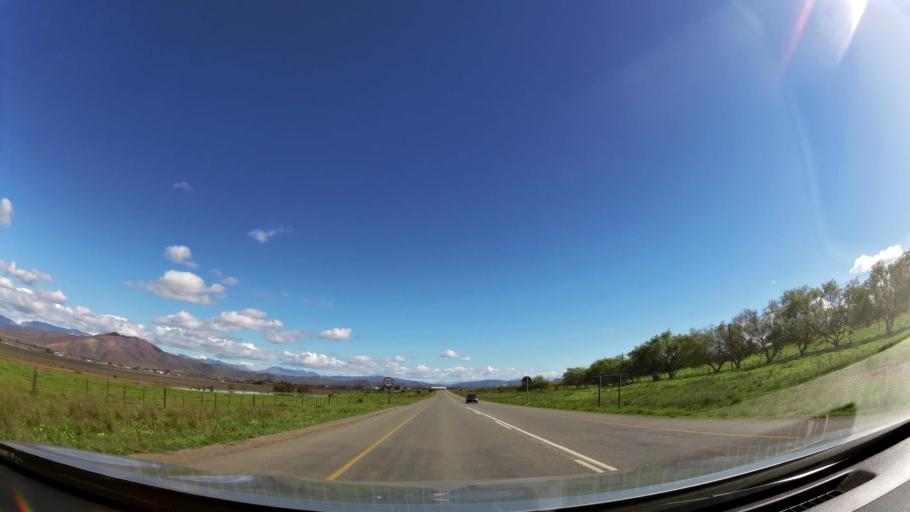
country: ZA
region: Western Cape
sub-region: Cape Winelands District Municipality
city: Ashton
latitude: -33.8383
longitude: 20.0279
